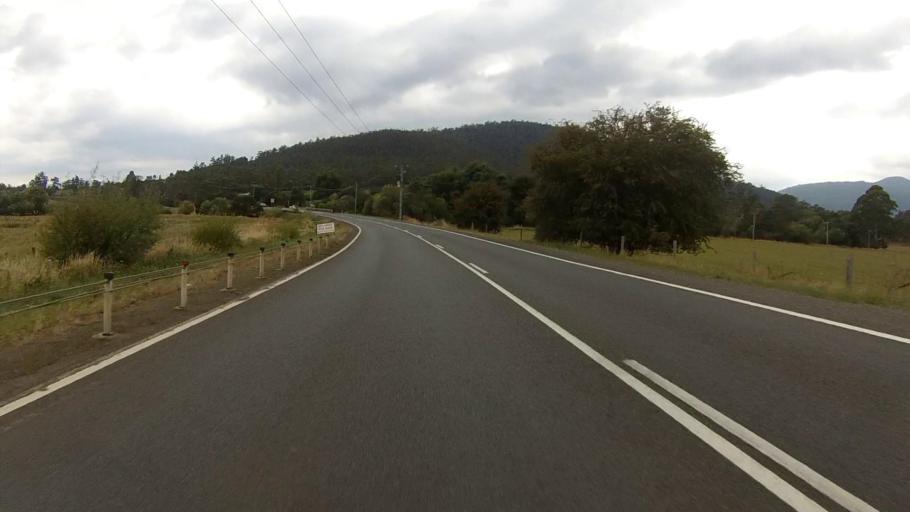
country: AU
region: Tasmania
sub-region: Huon Valley
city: Franklin
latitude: -43.0713
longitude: 147.0395
